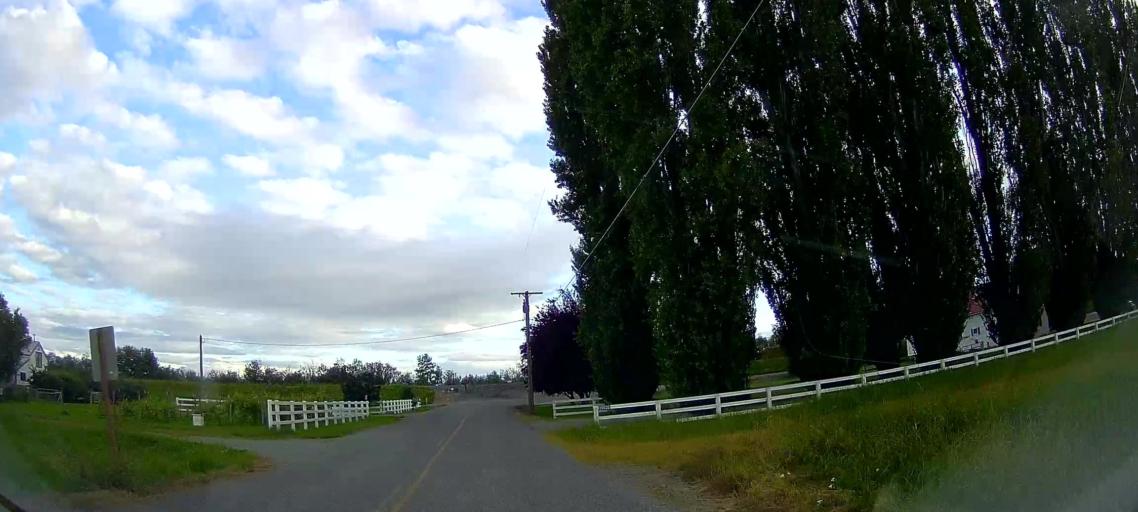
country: US
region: Washington
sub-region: Skagit County
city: Mount Vernon
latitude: 48.3700
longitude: -122.4005
